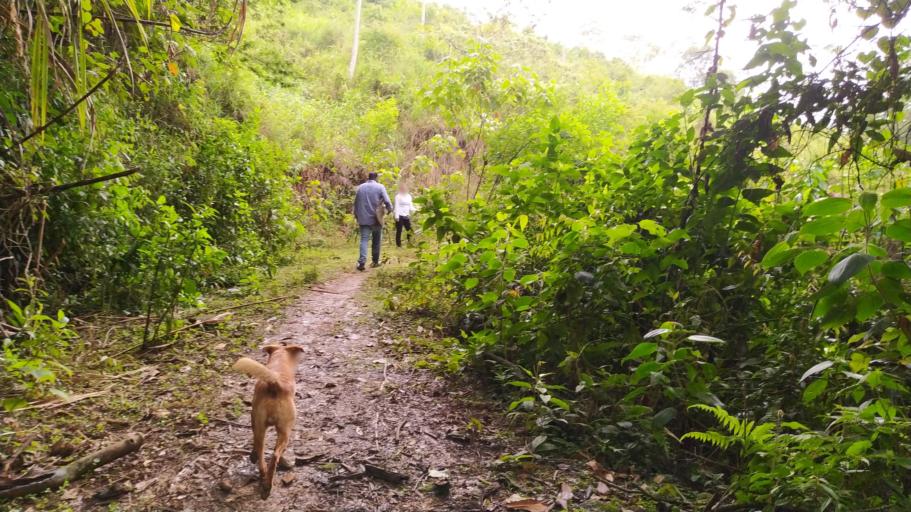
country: CO
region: Valle del Cauca
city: Jamundi
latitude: 3.3190
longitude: -76.5866
